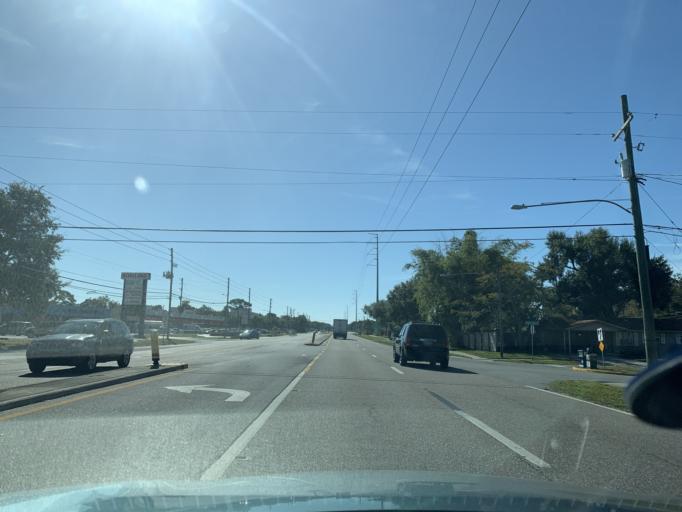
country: US
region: Florida
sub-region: Pinellas County
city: Largo
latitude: 27.8776
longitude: -82.7624
